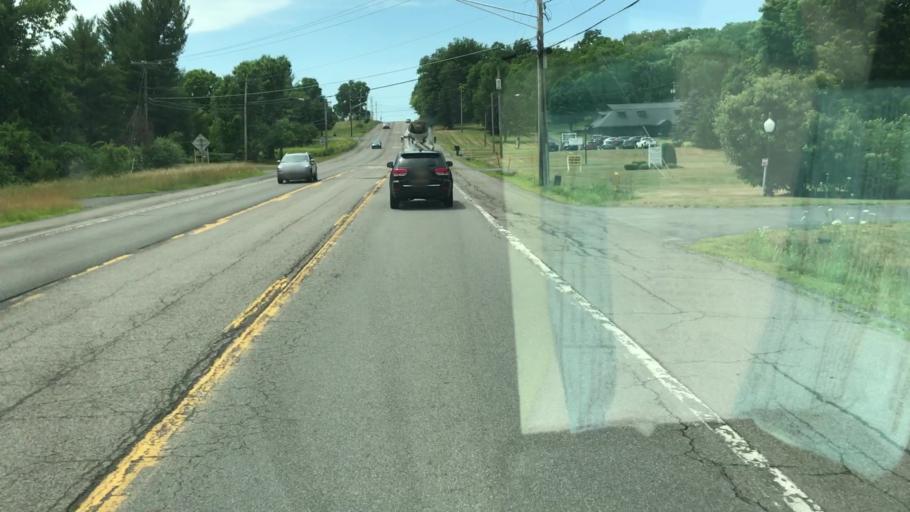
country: US
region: New York
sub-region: Onondaga County
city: Skaneateles
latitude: 42.9454
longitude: -76.3952
